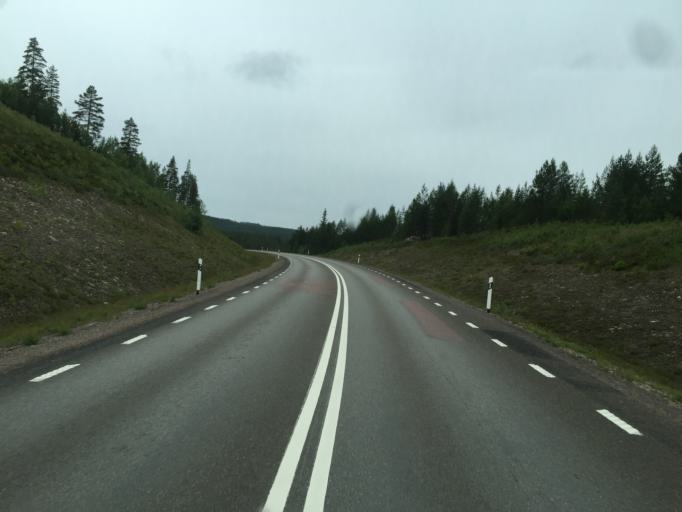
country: SE
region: Dalarna
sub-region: Malung-Saelens kommun
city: Malung
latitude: 60.6113
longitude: 13.5937
